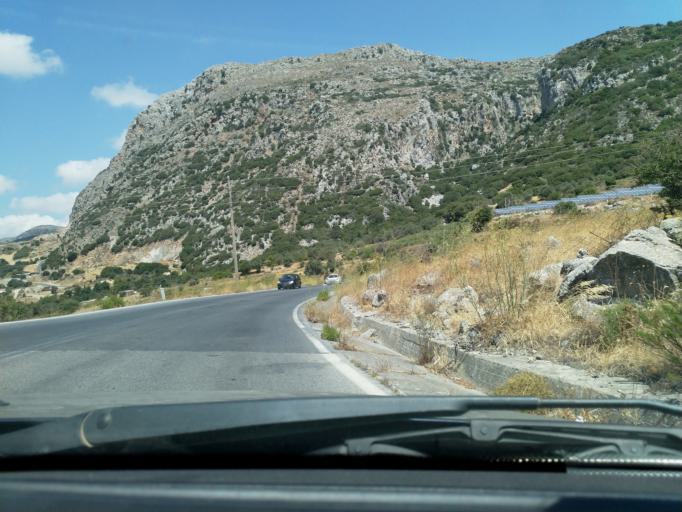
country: GR
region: Crete
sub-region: Nomos Rethymnis
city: Agia Foteini
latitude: 35.2002
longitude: 24.5434
